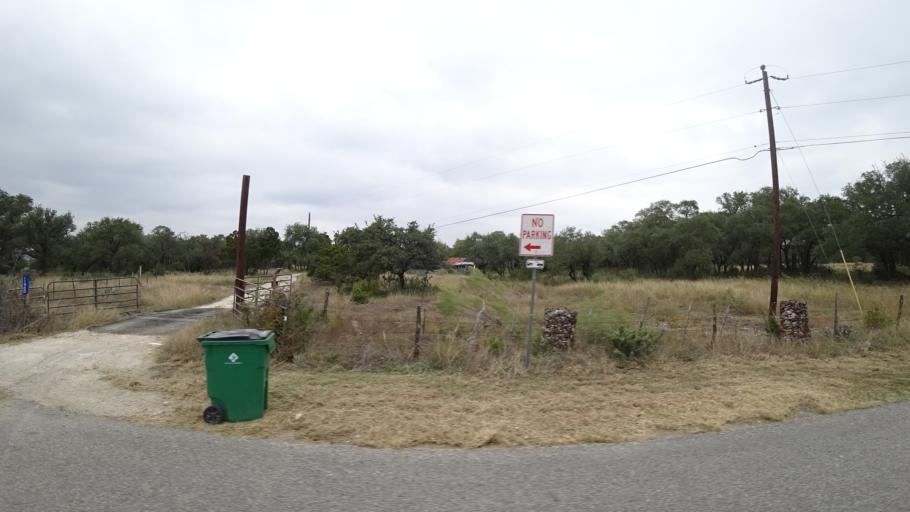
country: US
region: Texas
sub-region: Williamson County
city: Anderson Mill
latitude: 30.4439
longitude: -97.8352
